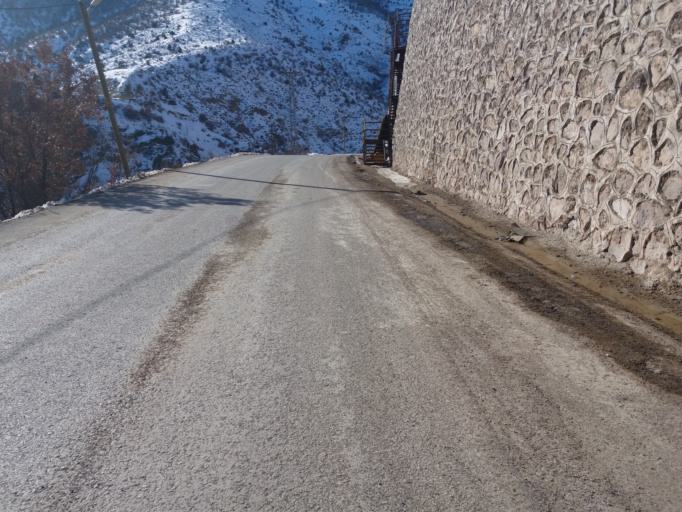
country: TR
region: Gumushane
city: Gumushkhane
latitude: 40.4403
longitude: 39.5009
